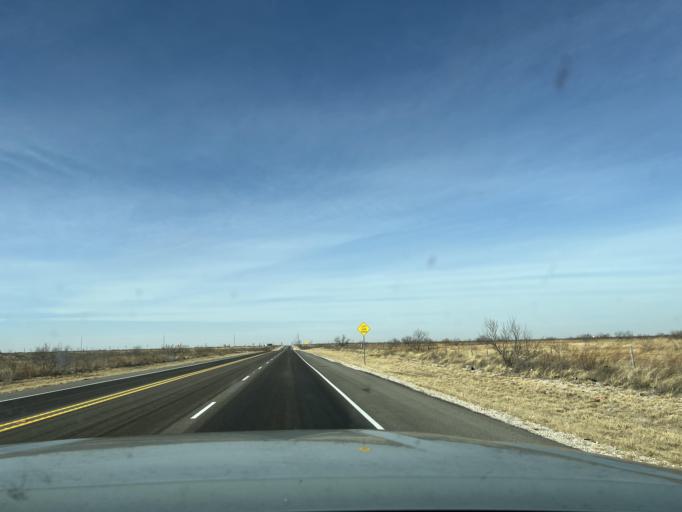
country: US
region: Texas
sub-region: Andrews County
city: Andrews
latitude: 32.3310
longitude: -102.6445
